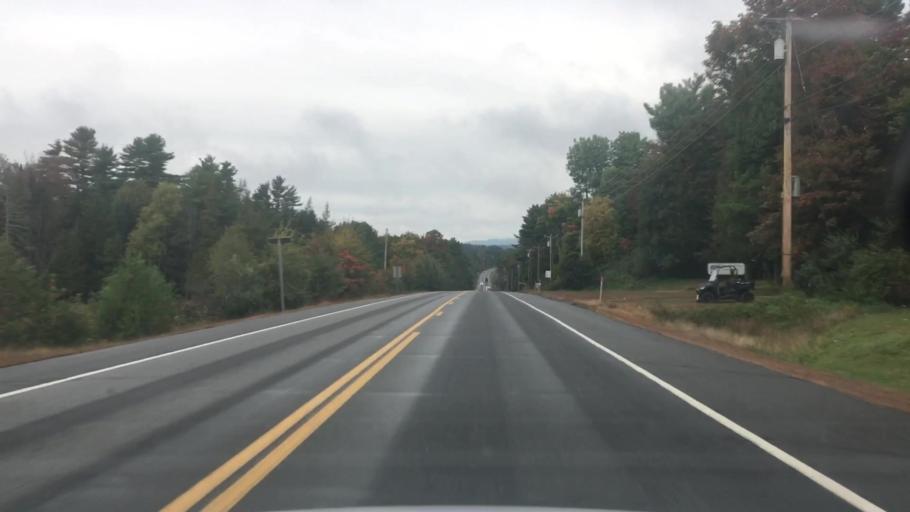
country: US
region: Maine
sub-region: Kennebec County
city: Belgrade
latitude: 44.3972
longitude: -69.8042
